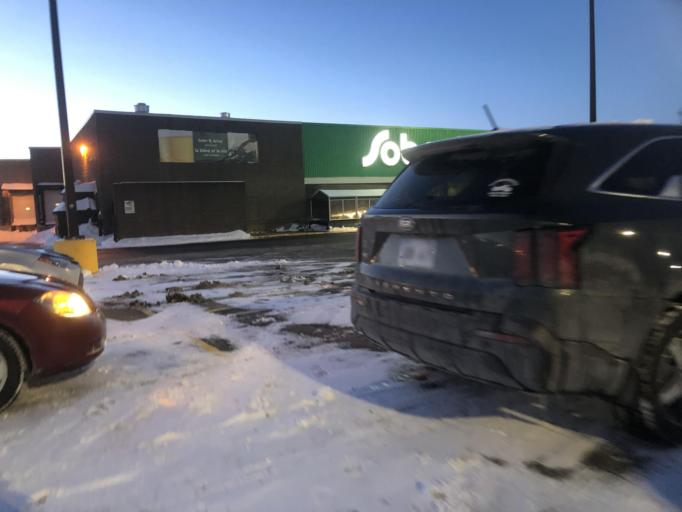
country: CA
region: New Brunswick
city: Saint John
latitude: 45.2794
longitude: -66.0779
